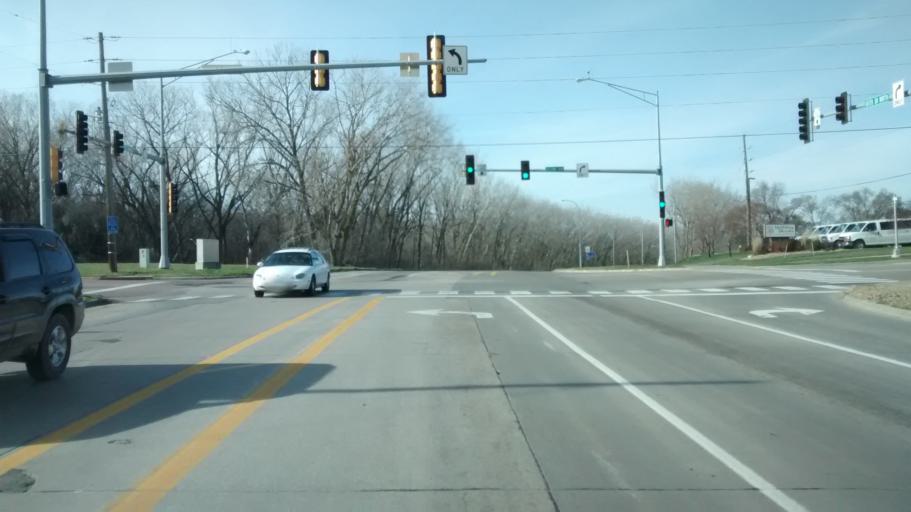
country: US
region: Iowa
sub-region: Woodbury County
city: Sioux City
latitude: 42.5407
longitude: -96.3935
